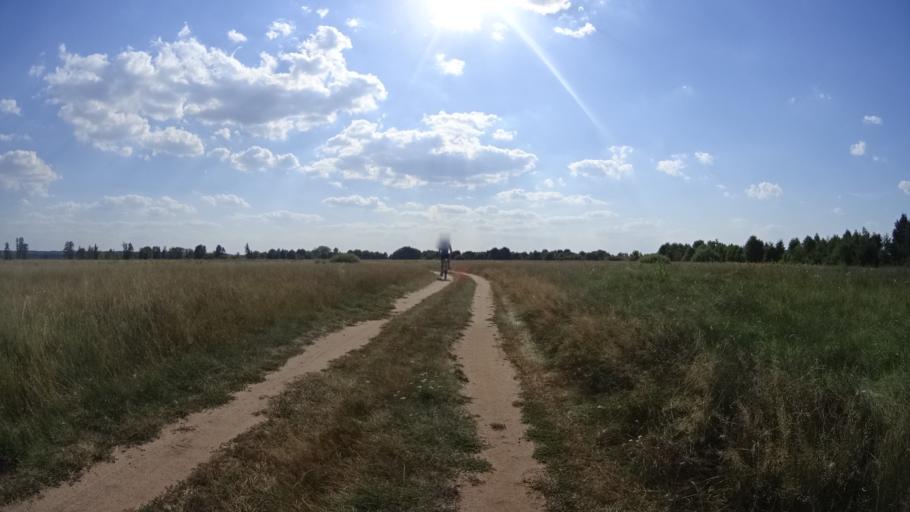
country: PL
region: Masovian Voivodeship
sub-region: Powiat bialobrzeski
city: Wysmierzyce
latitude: 51.6476
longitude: 20.8249
